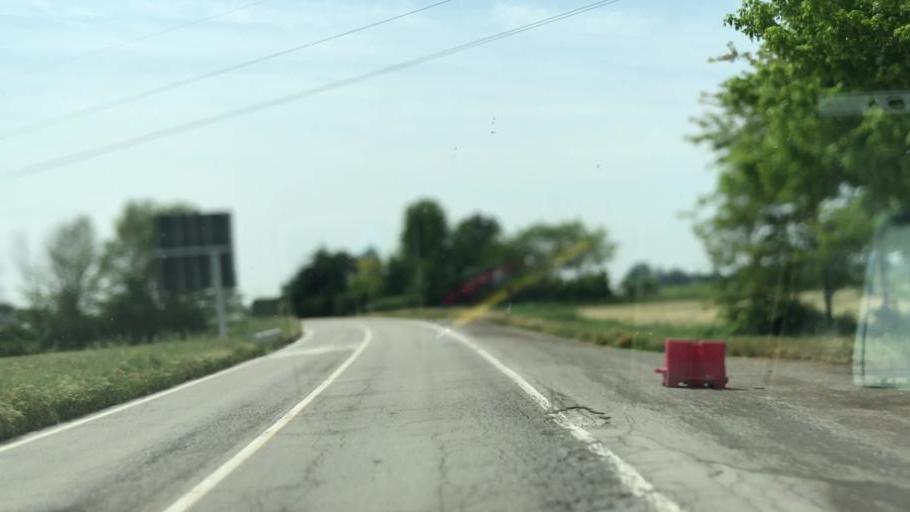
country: IT
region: Lombardy
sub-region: Provincia di Mantova
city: Campitello
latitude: 45.0821
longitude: 10.5983
